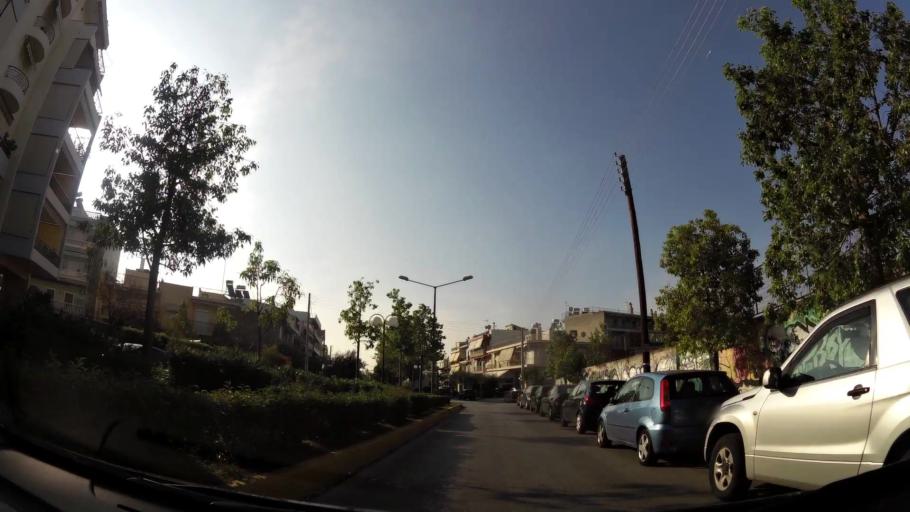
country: GR
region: Attica
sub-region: Nomarchia Athinas
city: Agios Dimitrios
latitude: 37.9306
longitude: 23.7472
